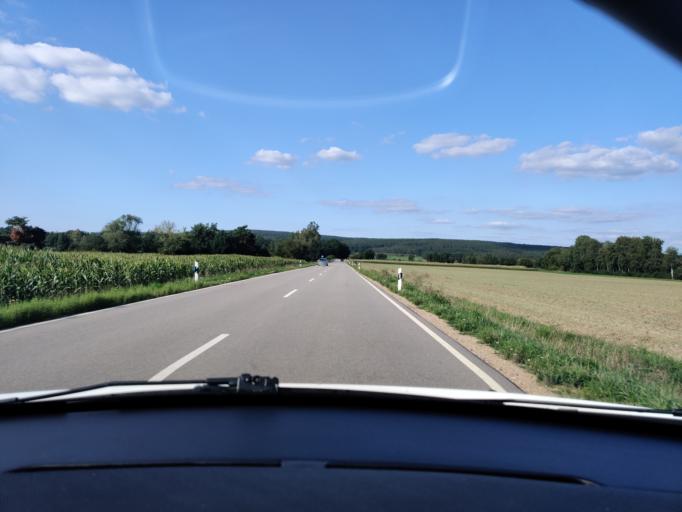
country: DE
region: Bavaria
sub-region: Upper Palatinate
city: Schwarzenfeld
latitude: 49.3644
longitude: 12.1563
